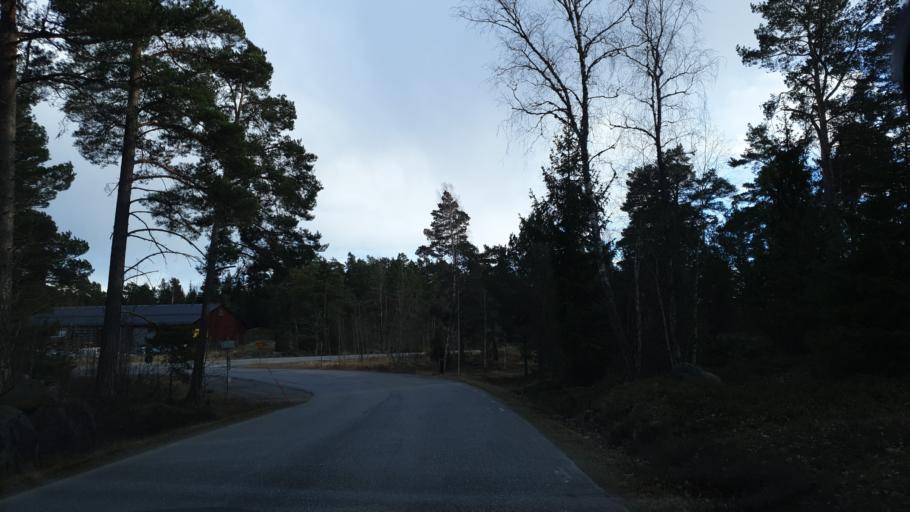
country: SE
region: Stockholm
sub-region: Varmdo Kommun
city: Holo
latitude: 59.3533
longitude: 18.7028
